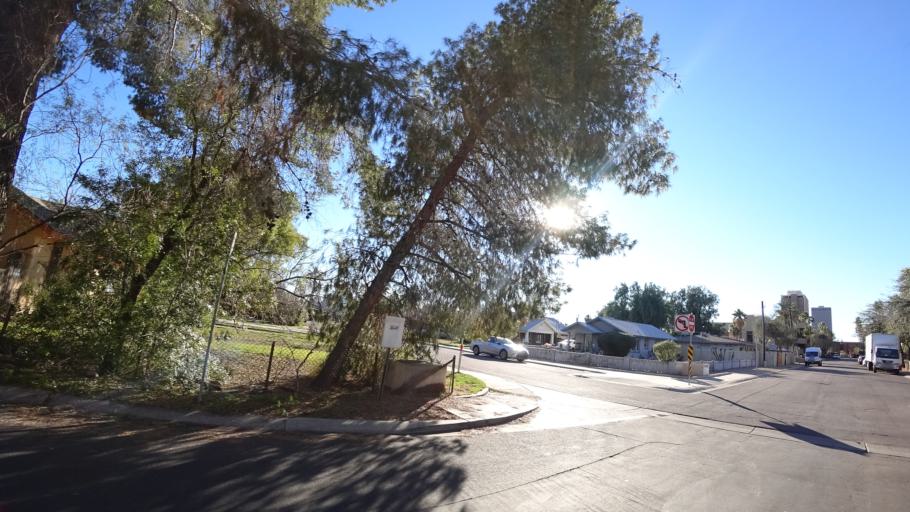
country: US
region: Arizona
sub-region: Maricopa County
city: Phoenix
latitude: 33.4928
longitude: -112.0663
